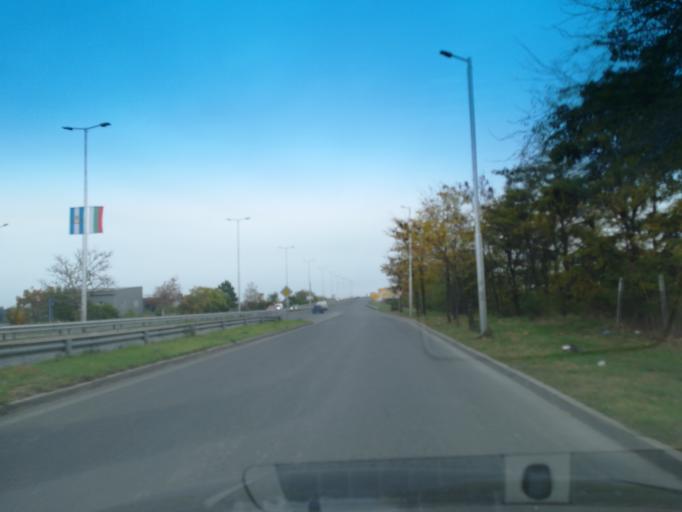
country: BG
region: Plovdiv
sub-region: Obshtina Plovdiv
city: Plovdiv
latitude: 42.1476
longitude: 24.8002
